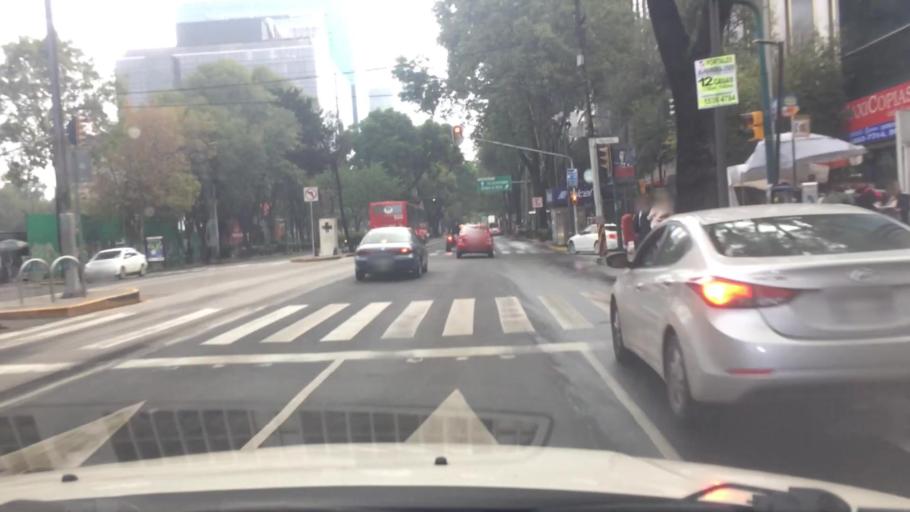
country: MX
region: Mexico City
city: Alvaro Obregon
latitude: 19.3594
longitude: -99.1835
